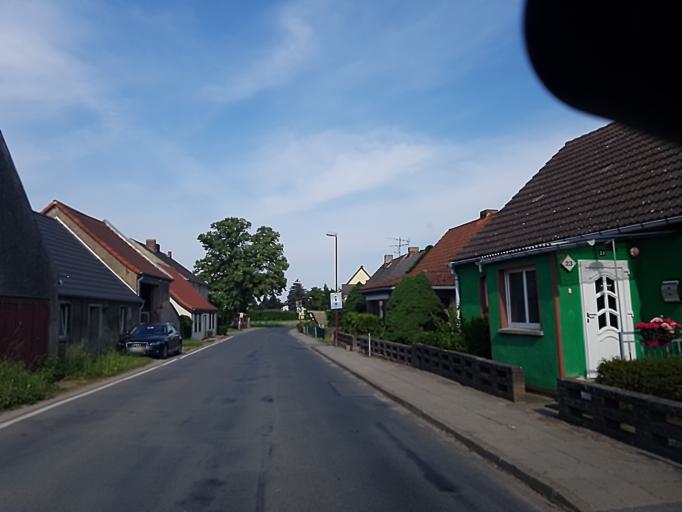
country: DE
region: Brandenburg
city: Wiesenburg
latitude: 52.1082
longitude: 12.3972
